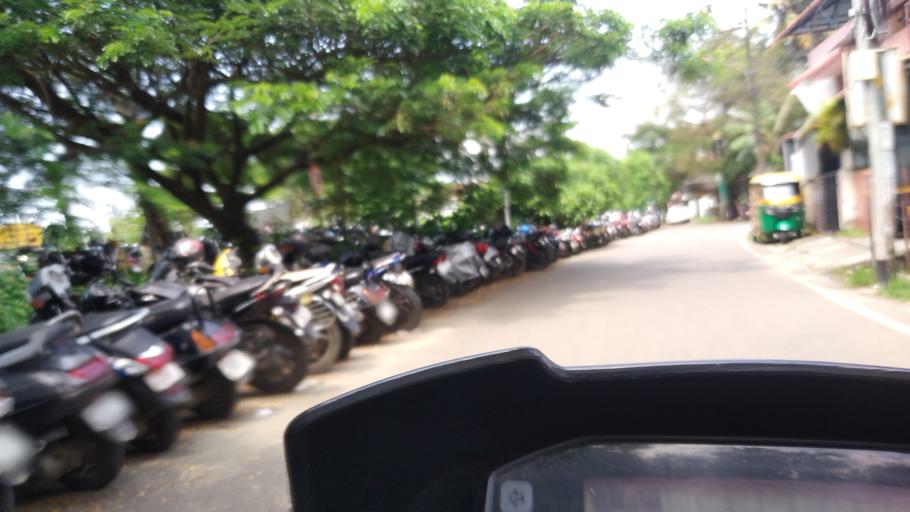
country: IN
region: Kerala
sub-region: Ernakulam
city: Cochin
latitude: 9.9701
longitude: 76.2921
